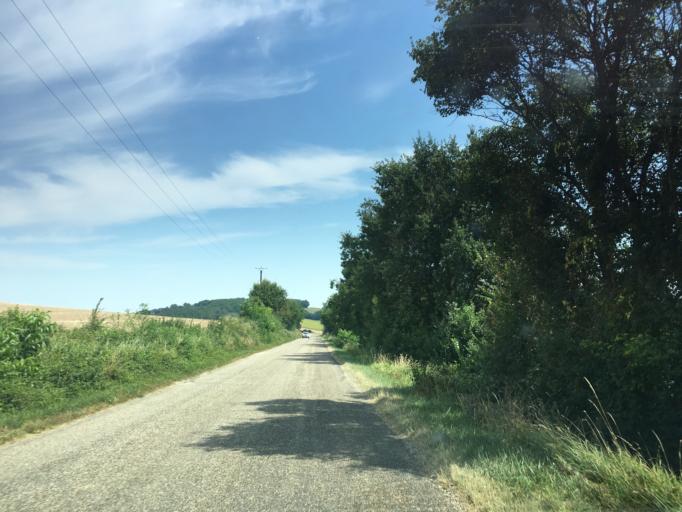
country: FR
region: Midi-Pyrenees
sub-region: Departement du Gers
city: Jegun
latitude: 43.8095
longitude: 0.5054
